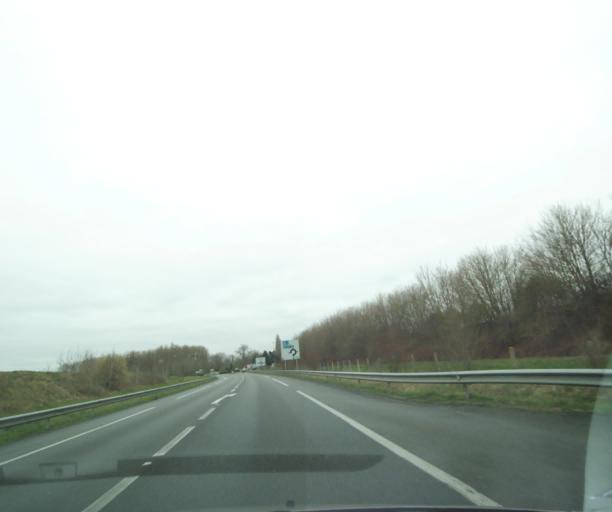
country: FR
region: Picardie
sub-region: Departement de l'Oise
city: Noyon
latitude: 49.5710
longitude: 3.0229
